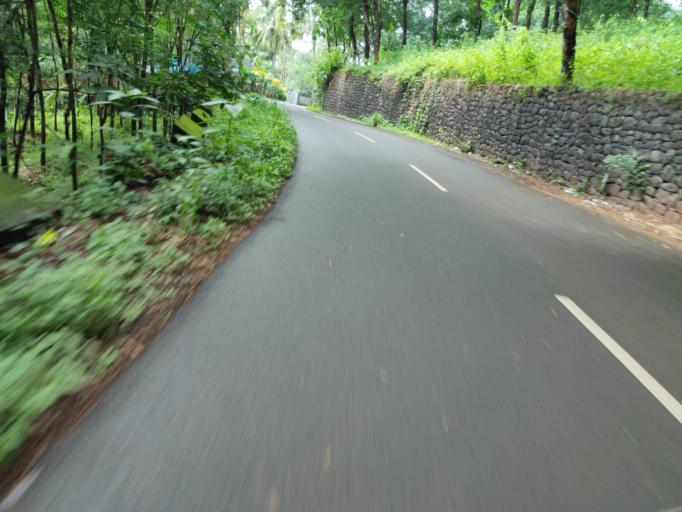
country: IN
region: Kerala
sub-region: Malappuram
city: Manjeri
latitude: 11.1406
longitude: 76.1322
